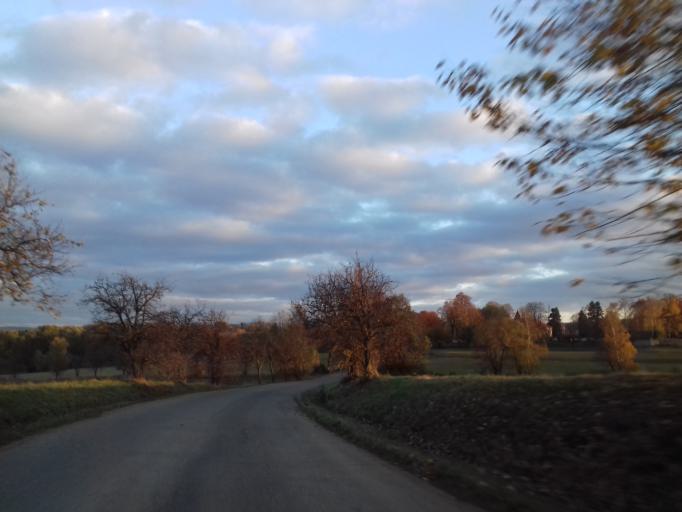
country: CZ
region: Pardubicky
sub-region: Okres Chrudim
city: Skutec
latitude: 49.8020
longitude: 15.9618
